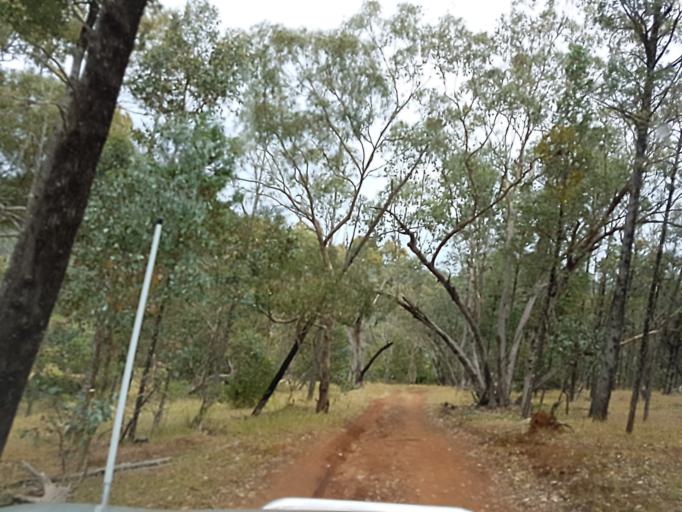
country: AU
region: New South Wales
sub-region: Snowy River
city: Jindabyne
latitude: -36.9364
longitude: 148.3999
